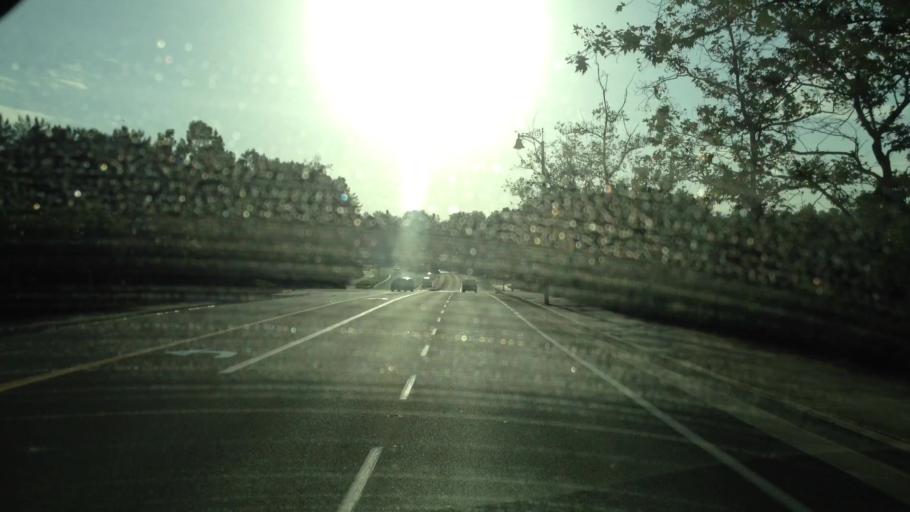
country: US
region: California
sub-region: Orange County
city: Rancho Santa Margarita
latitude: 33.6451
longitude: -117.6264
